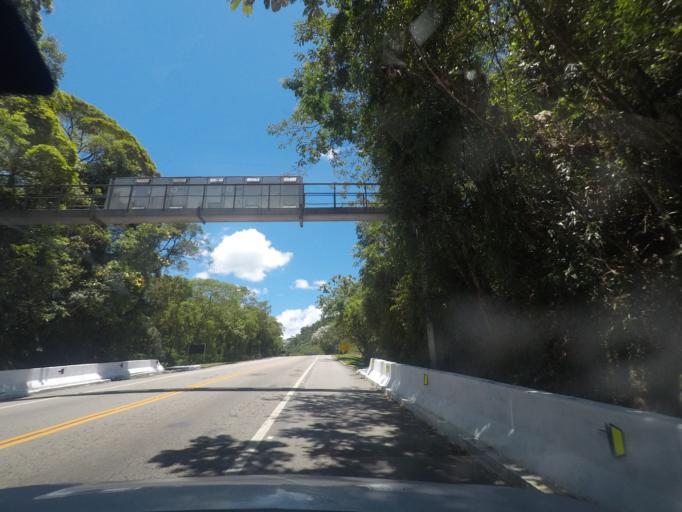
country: BR
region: Rio de Janeiro
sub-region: Teresopolis
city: Teresopolis
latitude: -22.4615
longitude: -42.9833
